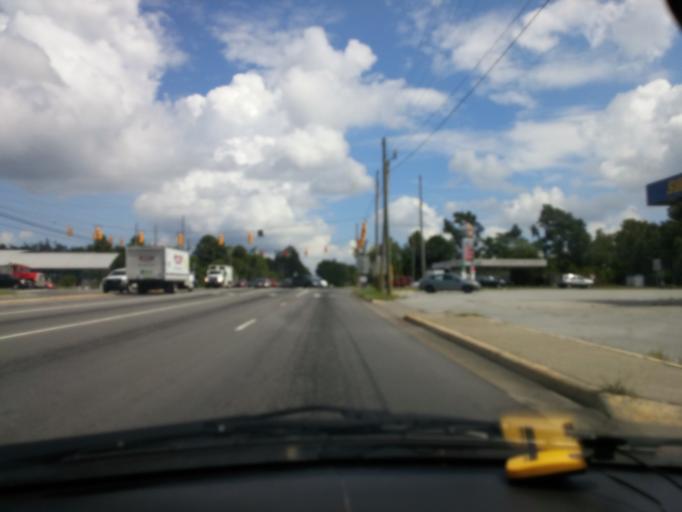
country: US
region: North Carolina
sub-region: Lenoir County
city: Kinston
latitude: 35.2539
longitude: -77.6023
